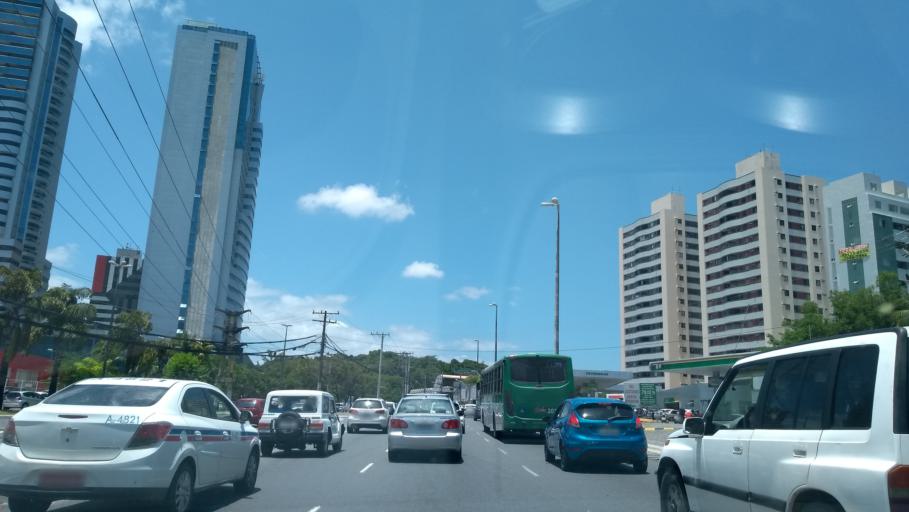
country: BR
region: Bahia
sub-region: Salvador
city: Salvador
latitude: -12.9826
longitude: -38.4504
